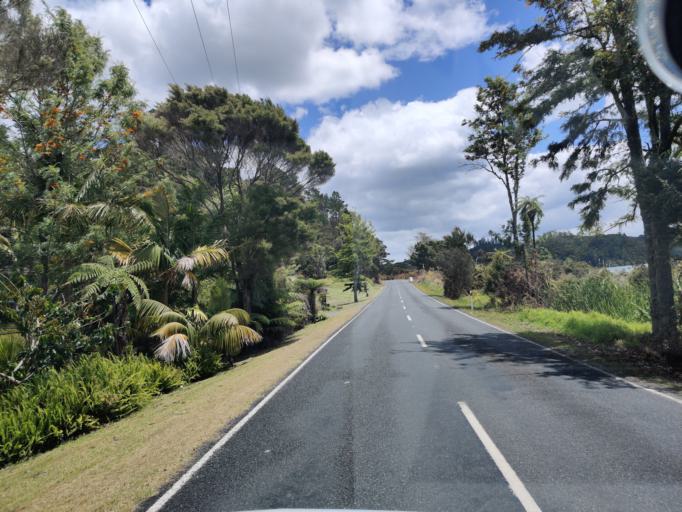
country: NZ
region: Northland
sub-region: Far North District
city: Paihia
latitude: -35.2904
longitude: 174.1443
